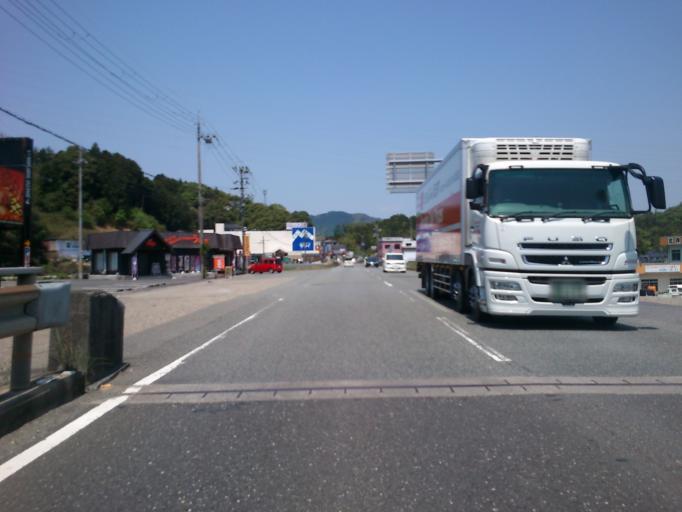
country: JP
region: Kyoto
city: Fukuchiyama
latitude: 35.3084
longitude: 135.1033
